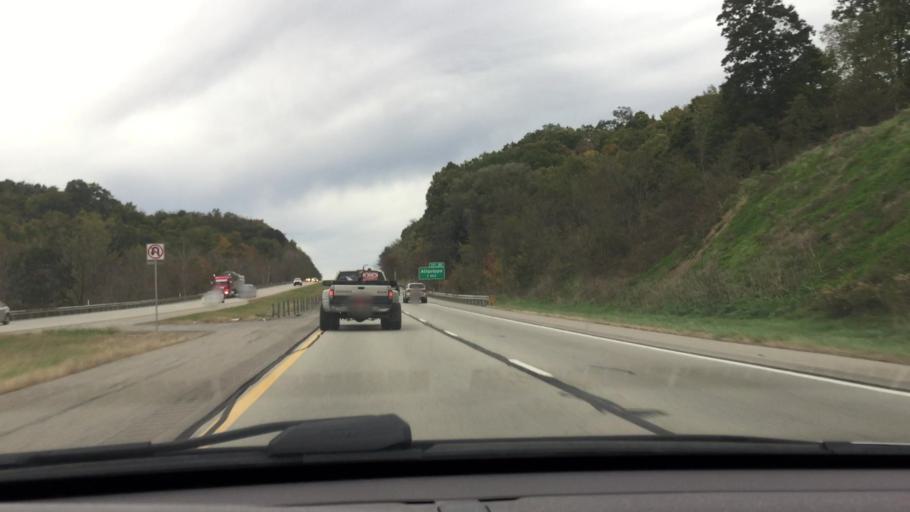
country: US
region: Pennsylvania
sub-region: Beaver County
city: Ambridge
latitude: 40.5819
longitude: -80.2908
